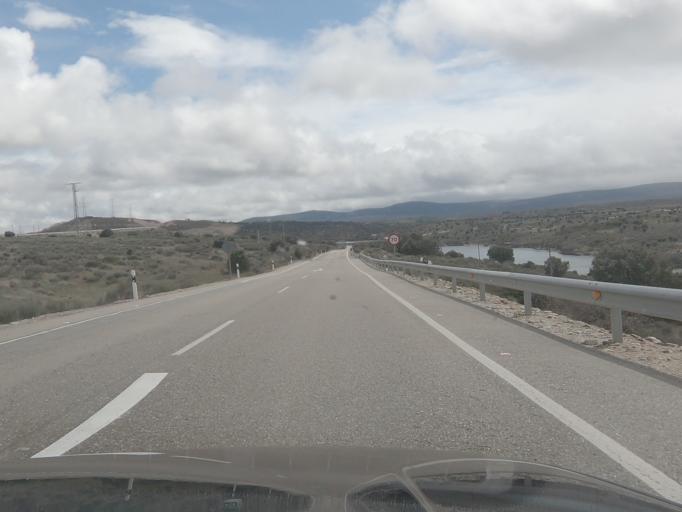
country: ES
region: Castille and Leon
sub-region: Provincia de Zamora
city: Villardeciervos
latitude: 41.9903
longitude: -6.2416
